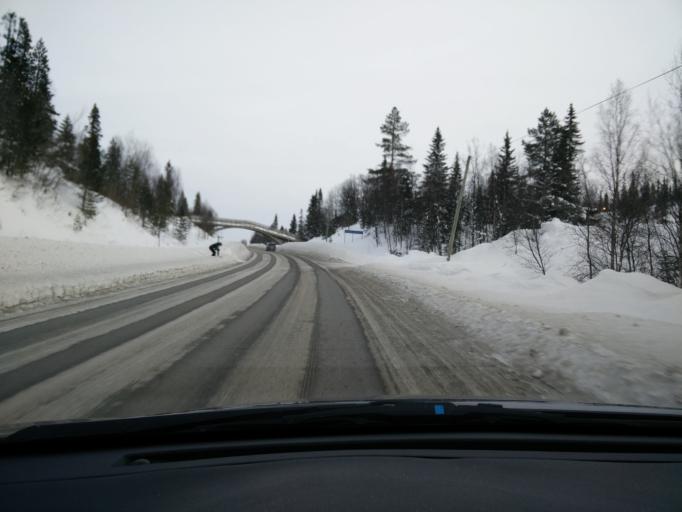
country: SE
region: Jaemtland
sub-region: Bergs Kommun
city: Hoverberg
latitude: 62.4860
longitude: 13.9658
